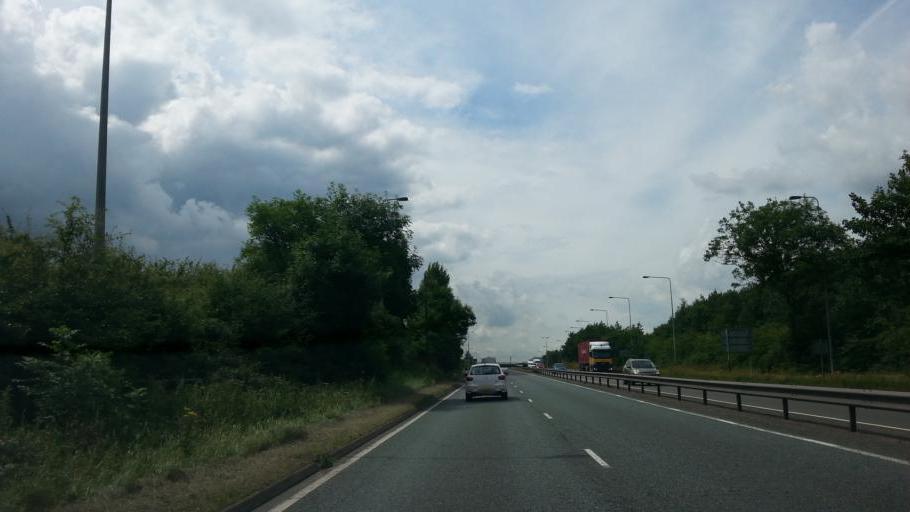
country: GB
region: England
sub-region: Staffordshire
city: Whittington
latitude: 52.7059
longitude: -1.7725
